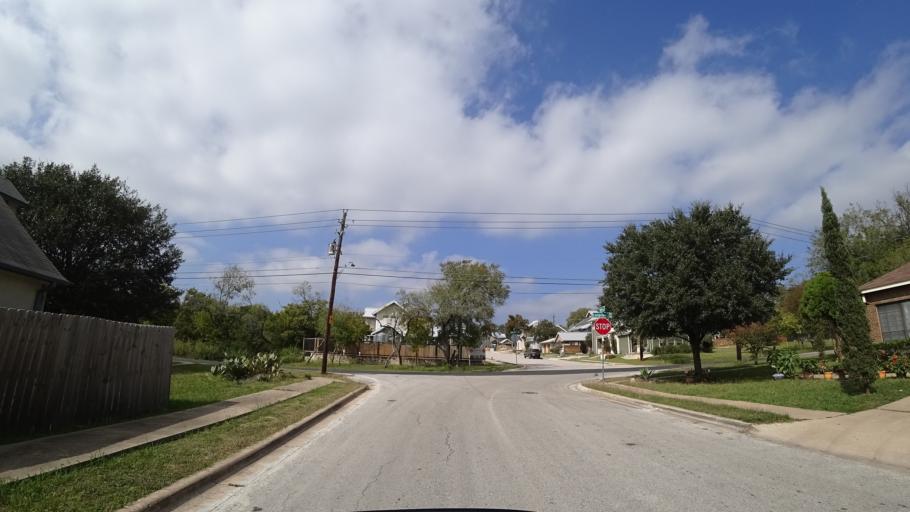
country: US
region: Texas
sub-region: Travis County
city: Shady Hollow
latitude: 30.1967
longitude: -97.8311
